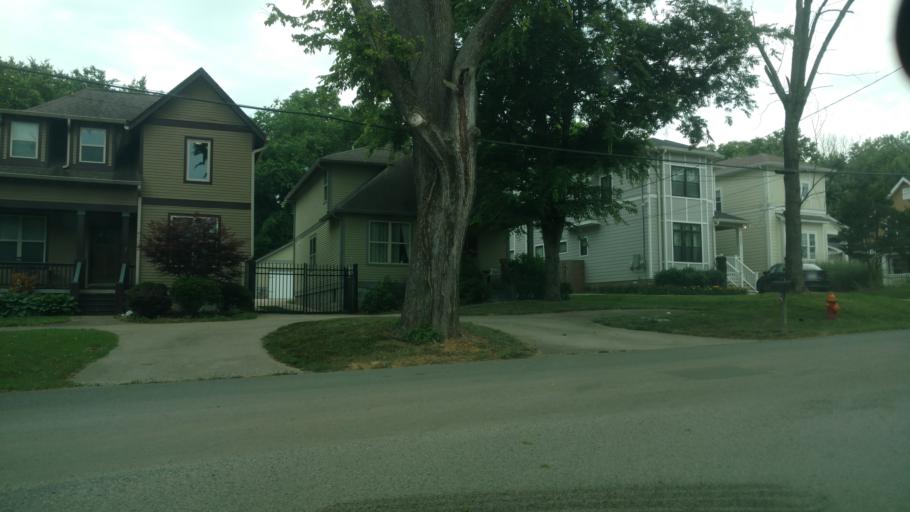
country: US
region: Tennessee
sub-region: Davidson County
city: Nashville
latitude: 36.1890
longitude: -86.7231
